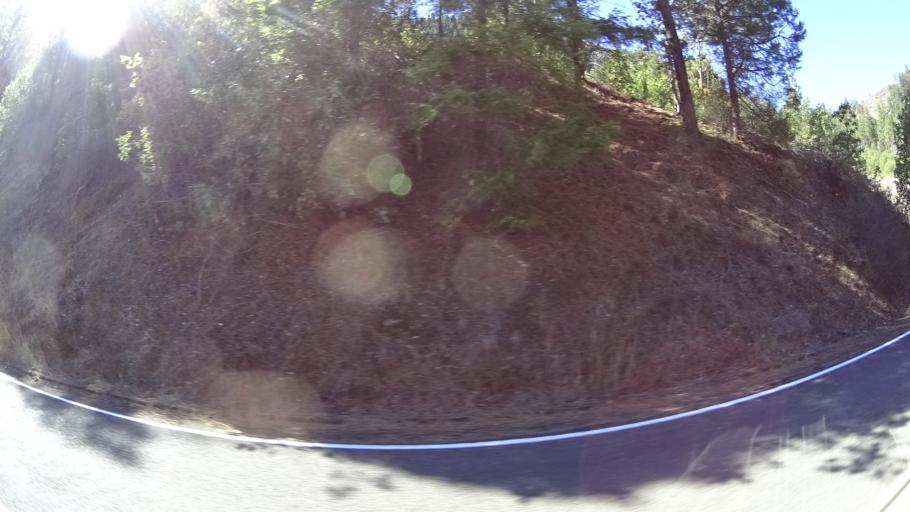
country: US
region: California
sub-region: Siskiyou County
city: Happy Camp
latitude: 41.3703
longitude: -123.4168
